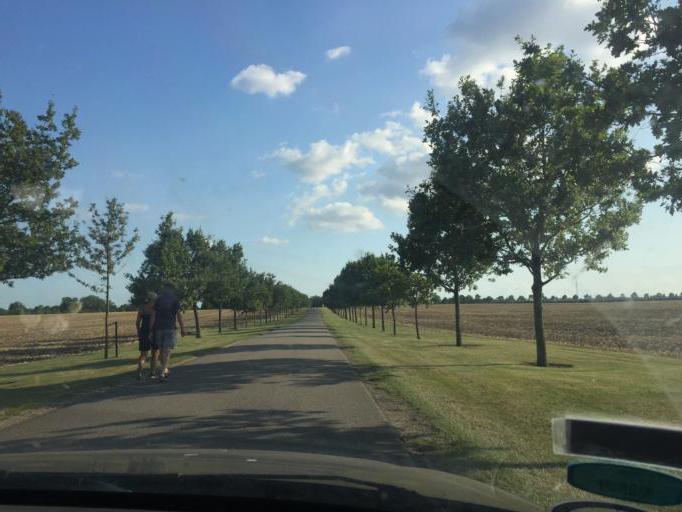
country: DK
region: Zealand
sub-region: Lolland Kommune
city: Maribo
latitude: 54.8050
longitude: 11.5086
